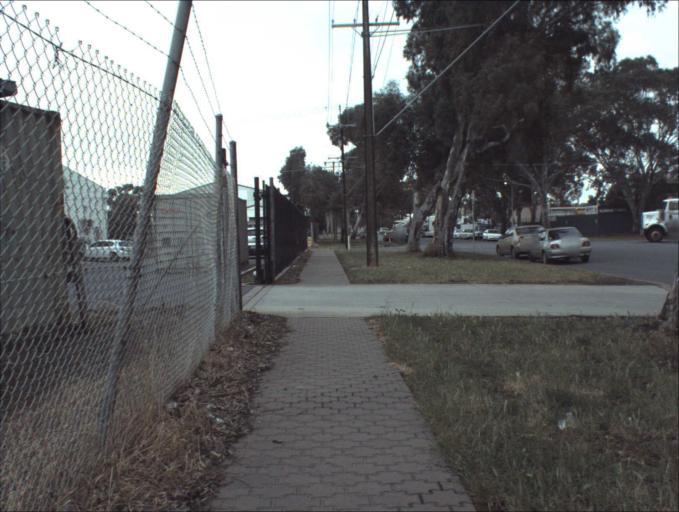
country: AU
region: South Australia
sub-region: Charles Sturt
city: Woodville North
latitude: -34.8462
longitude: 138.5535
